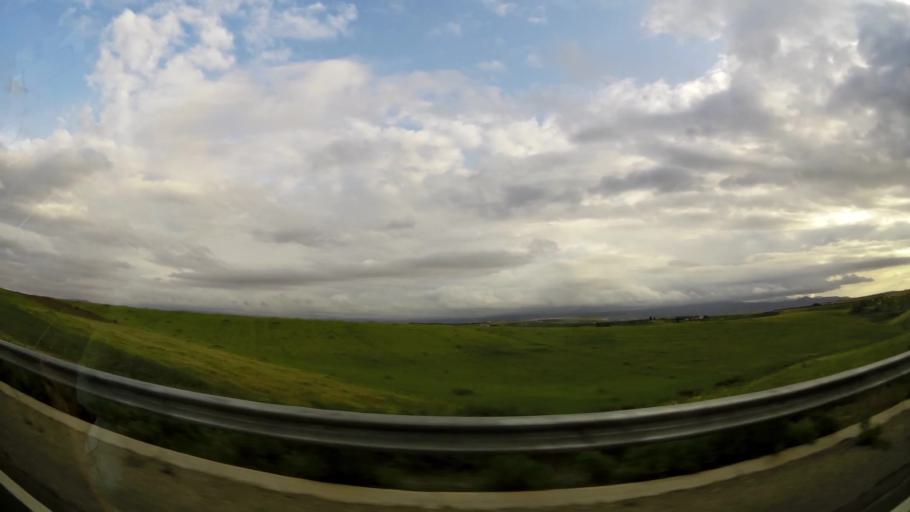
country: MA
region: Taza-Al Hoceima-Taounate
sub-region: Taza
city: Taza
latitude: 34.2521
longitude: -3.9222
